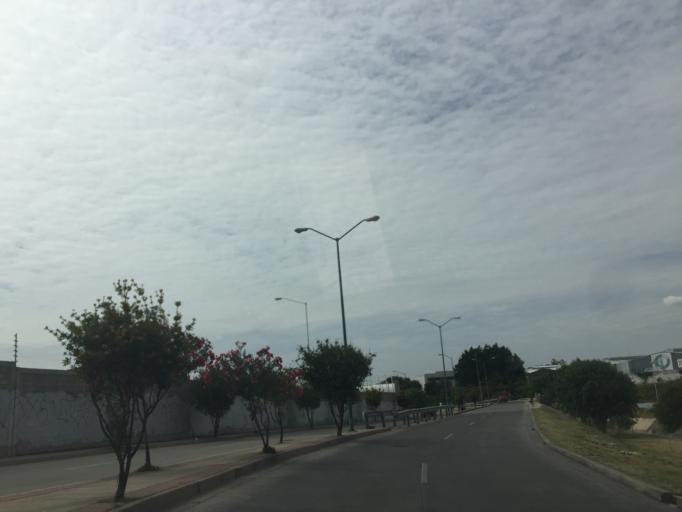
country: MX
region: Guanajuato
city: Leon
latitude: 21.1505
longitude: -101.6778
